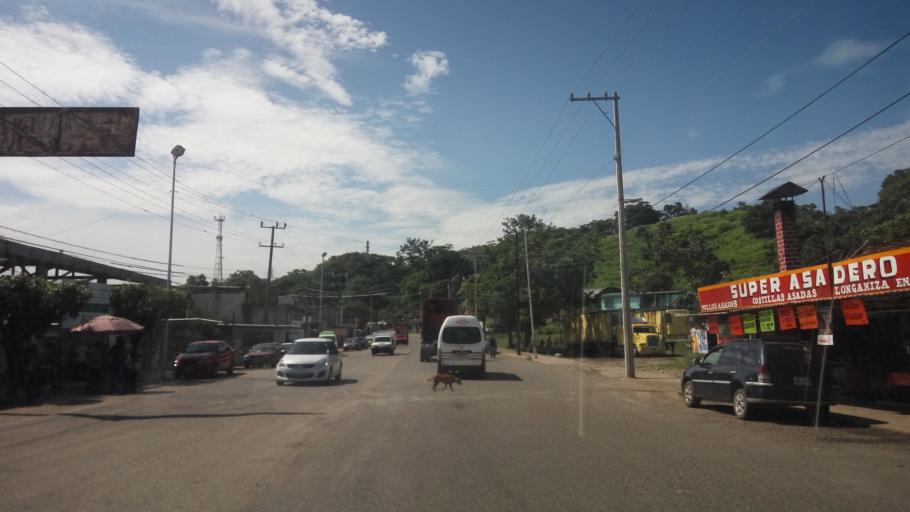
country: MX
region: Tabasco
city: Teapa
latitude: 17.5677
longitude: -92.9553
